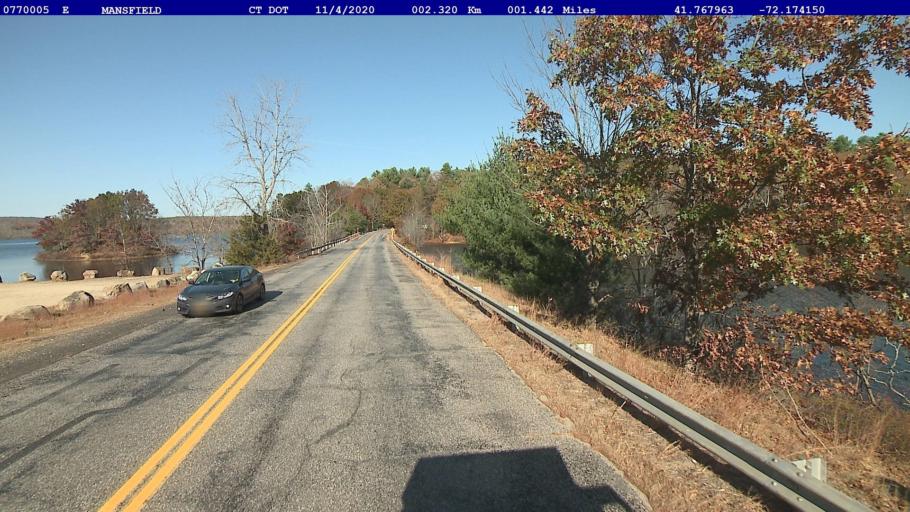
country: US
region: Connecticut
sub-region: Tolland County
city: Mansfield City
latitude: 41.7680
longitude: -72.1741
